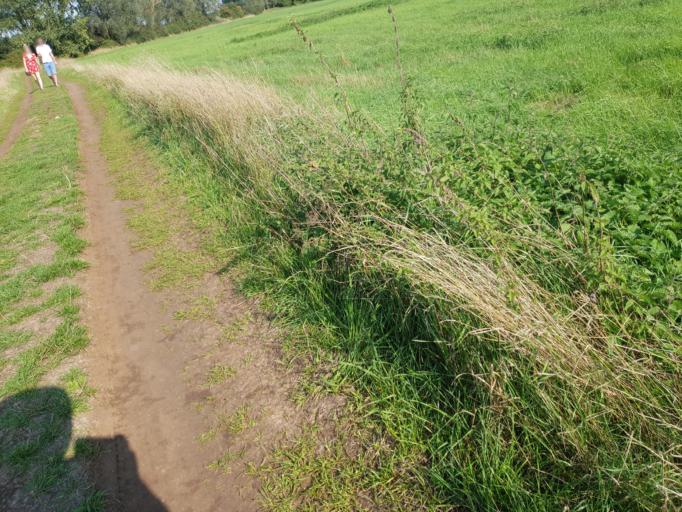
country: GB
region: England
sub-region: Suffolk
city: East Bergholt
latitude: 51.9530
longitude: 1.0201
